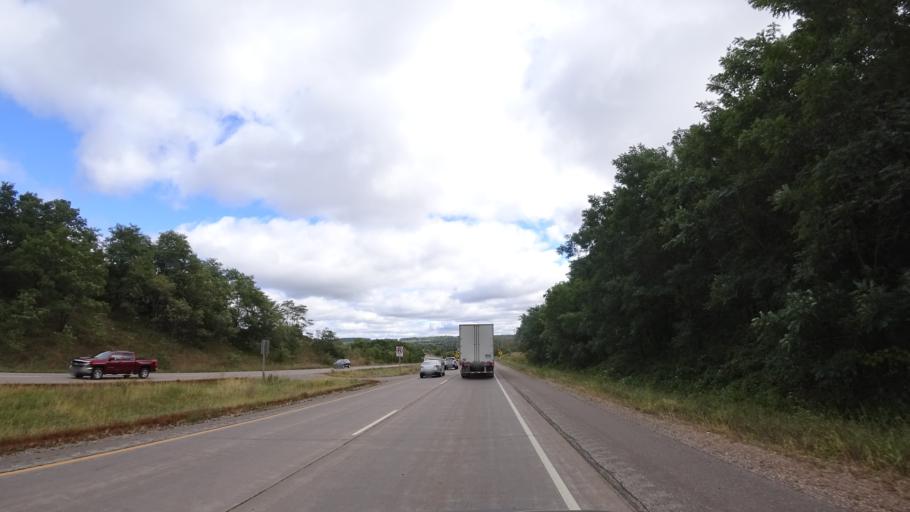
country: US
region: Wisconsin
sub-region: Eau Claire County
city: Eau Claire
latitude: 44.8418
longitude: -91.5148
